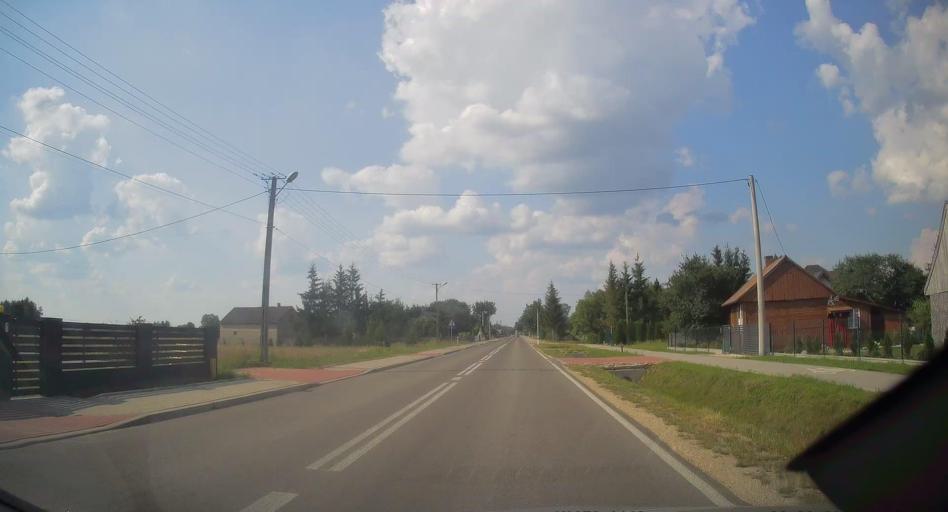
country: PL
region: Swietokrzyskie
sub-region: Powiat konecki
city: Radoszyce
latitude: 51.0469
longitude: 20.2834
